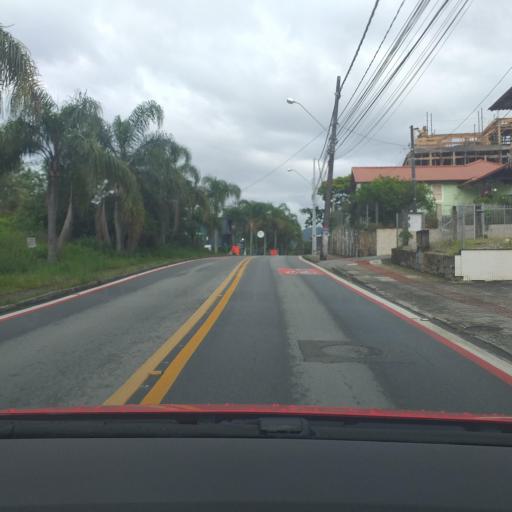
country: BR
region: Santa Catarina
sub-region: Florianopolis
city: Itacorubi
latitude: -27.5943
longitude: -48.4941
